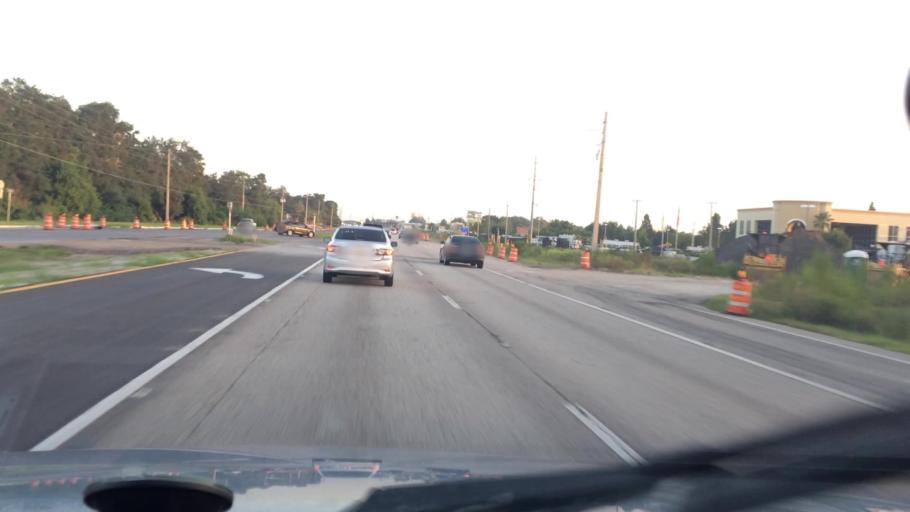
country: US
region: Florida
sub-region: Osceola County
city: Saint Cloud
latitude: 28.2702
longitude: -81.3369
